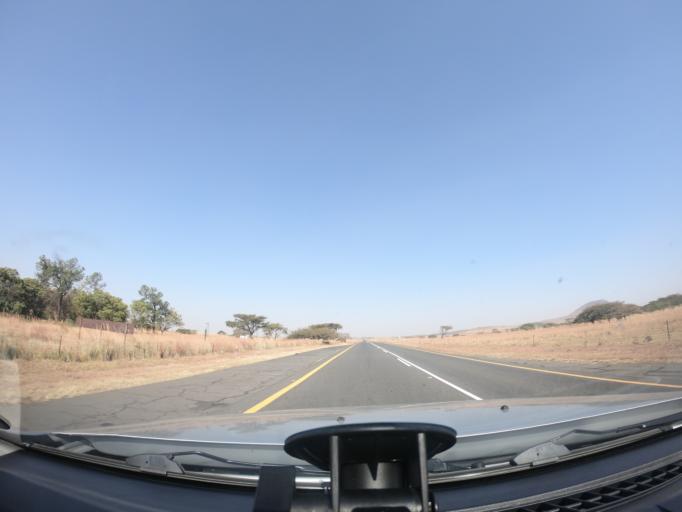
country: ZA
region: KwaZulu-Natal
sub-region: uThukela District Municipality
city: Ekuvukeni
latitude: -28.3683
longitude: 29.9521
